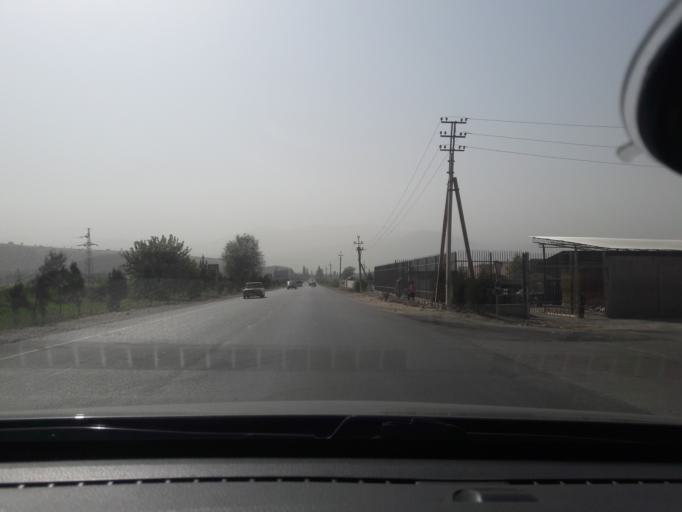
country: TJ
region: Republican Subordination
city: Vahdat
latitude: 38.5310
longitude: 69.0257
